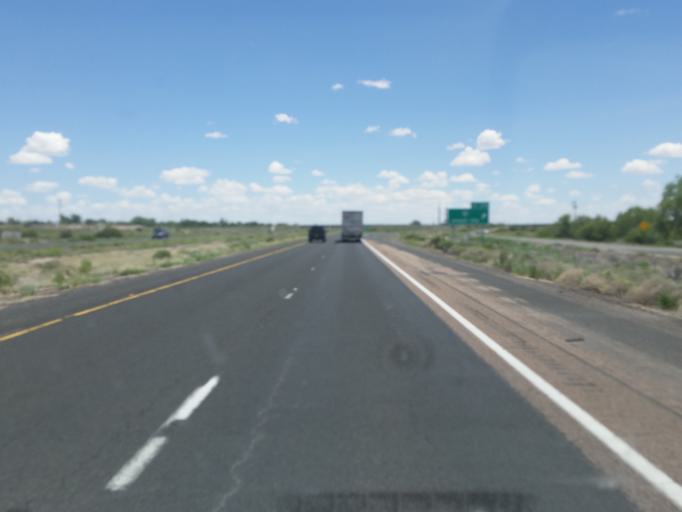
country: US
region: Arizona
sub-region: Navajo County
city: Joseph City
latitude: 34.9575
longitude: -110.3604
